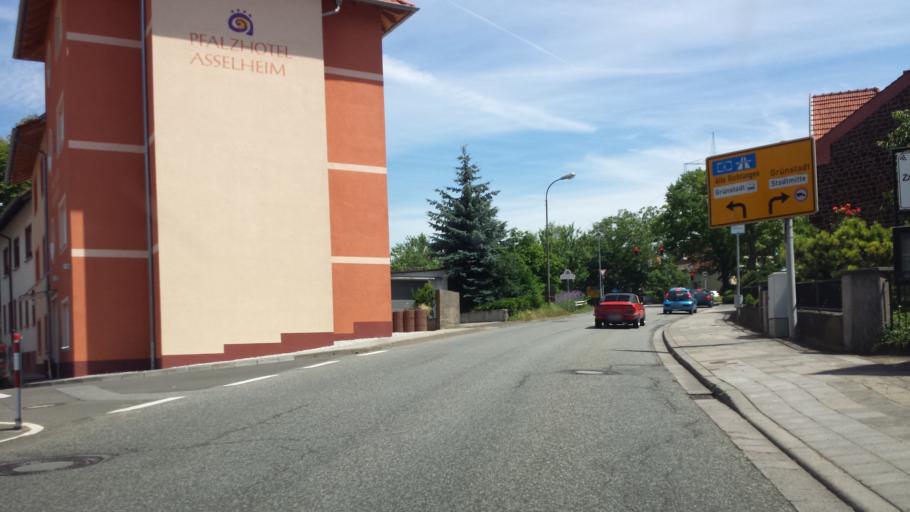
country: DE
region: Rheinland-Pfalz
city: Grunstadt
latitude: 49.5772
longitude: 8.1613
